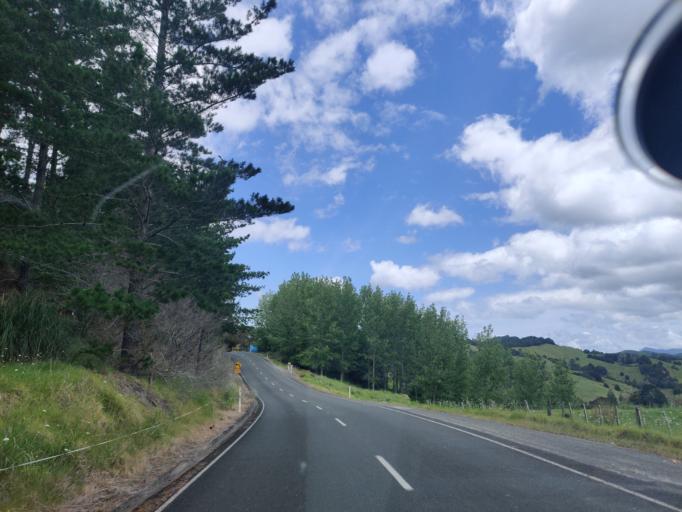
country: NZ
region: Northland
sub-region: Far North District
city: Kaitaia
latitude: -35.2839
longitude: 173.4844
